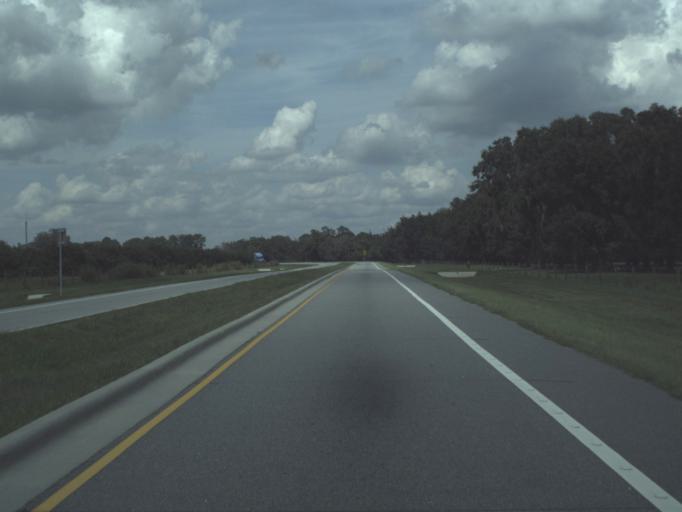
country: US
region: Florida
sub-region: Polk County
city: Wahneta
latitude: 27.9183
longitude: -81.7078
